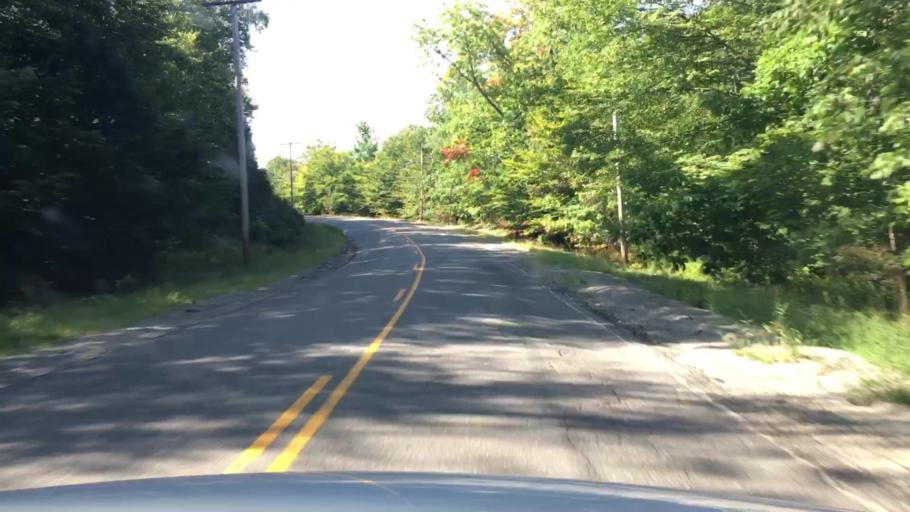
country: US
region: Maine
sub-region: Penobscot County
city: Enfield
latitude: 45.2241
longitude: -68.5387
